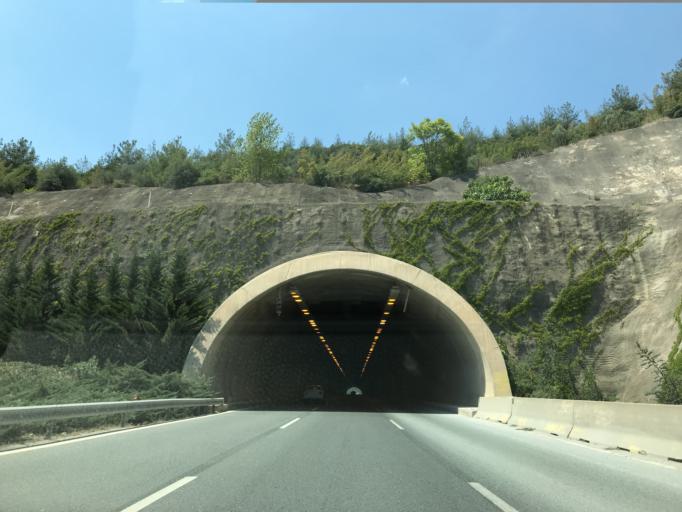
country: TR
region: Bursa
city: Gursu
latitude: 40.2541
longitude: 29.2181
